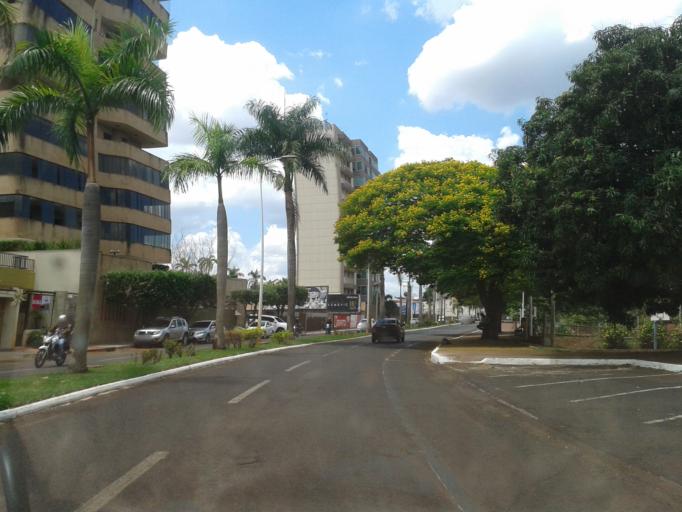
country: BR
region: Goias
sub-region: Itumbiara
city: Itumbiara
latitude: -18.4139
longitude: -49.2109
